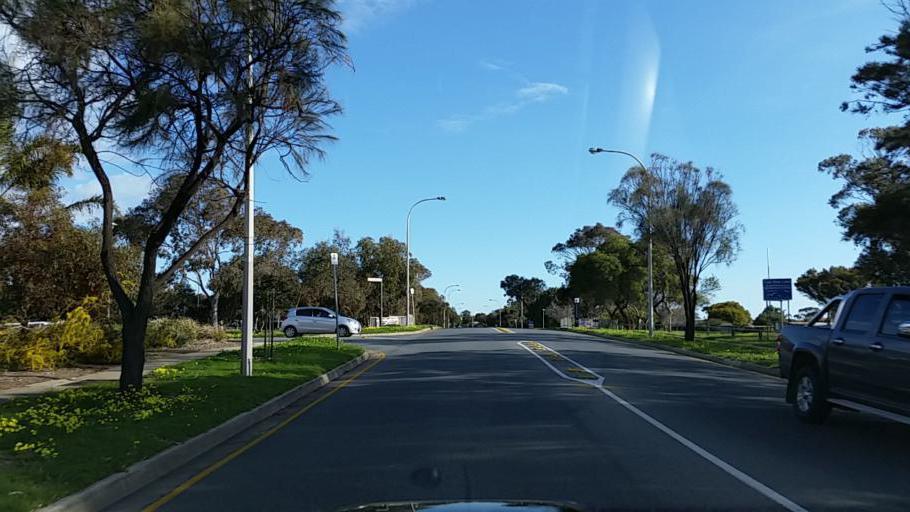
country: AU
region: South Australia
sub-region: Charles Sturt
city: West Lakes Shore
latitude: -34.8640
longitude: 138.4860
